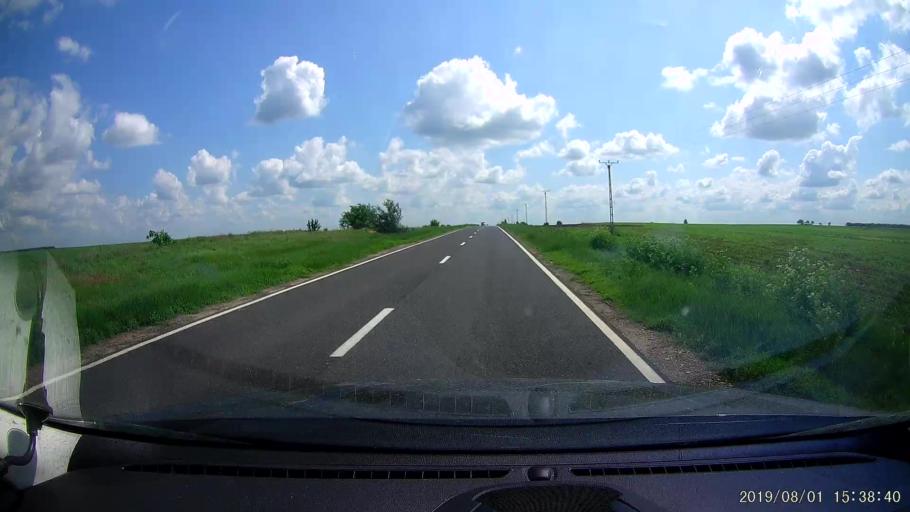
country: RO
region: Braila
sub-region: Comuna Insuratei
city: Insuratei
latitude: 44.8761
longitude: 27.5726
